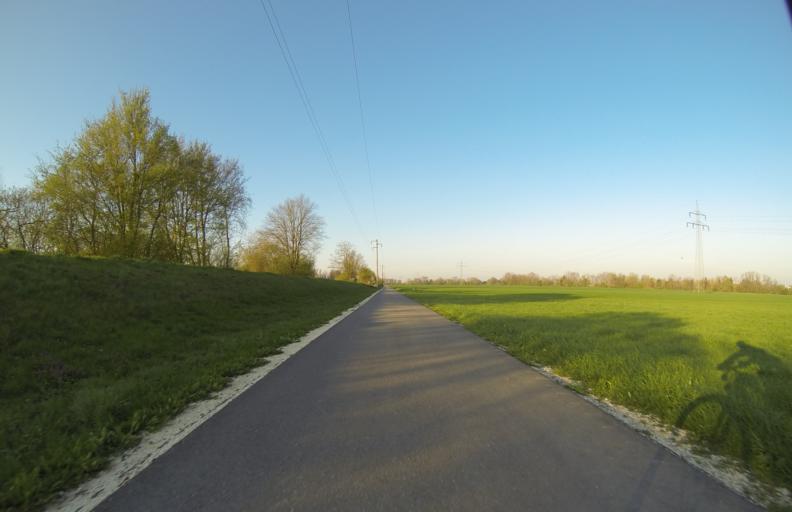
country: DE
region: Baden-Wuerttemberg
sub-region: Tuebingen Region
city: Erbach
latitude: 48.3416
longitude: 9.9376
